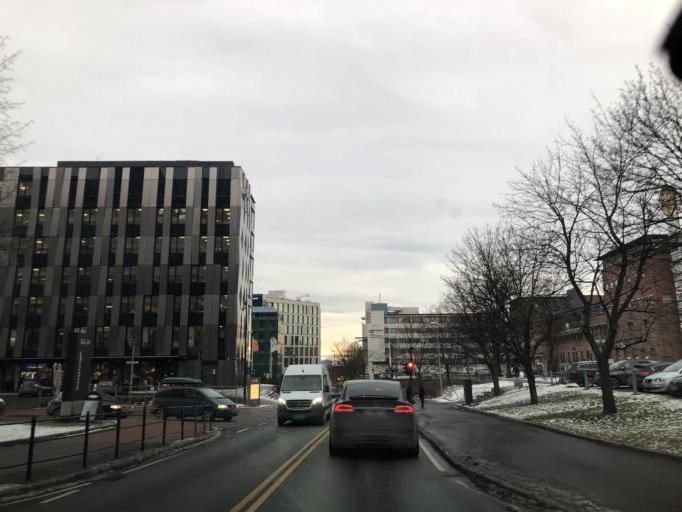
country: NO
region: Oslo
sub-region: Oslo
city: Oslo
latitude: 59.9139
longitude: 10.7995
